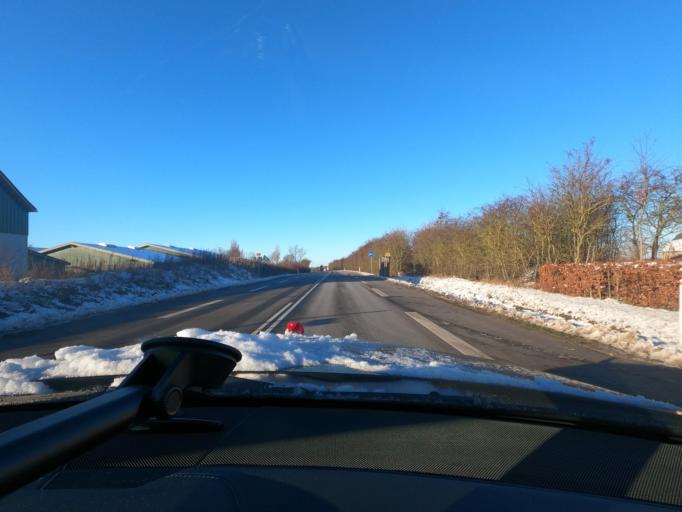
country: DK
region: South Denmark
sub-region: Sonderborg Kommune
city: Horuphav
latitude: 54.9019
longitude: 9.9511
